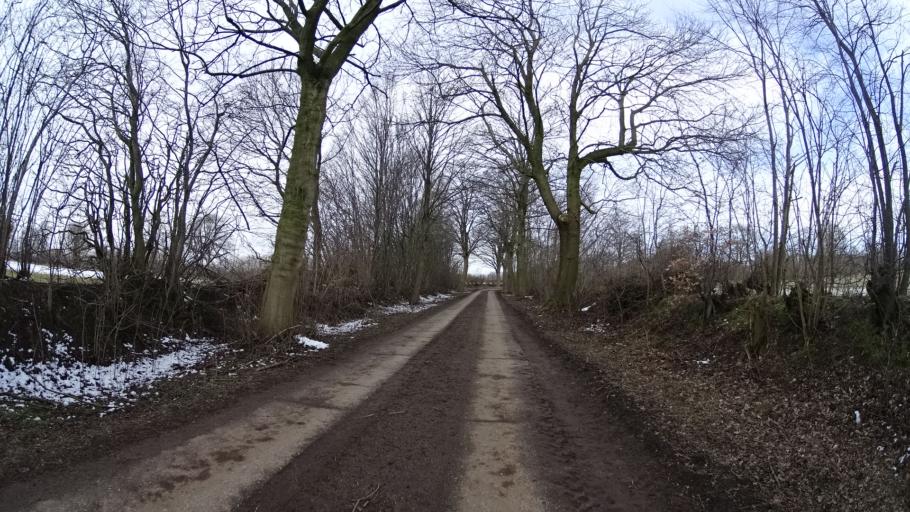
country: DE
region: Schleswig-Holstein
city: Rendswuhren
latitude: 54.0680
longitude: 10.1778
